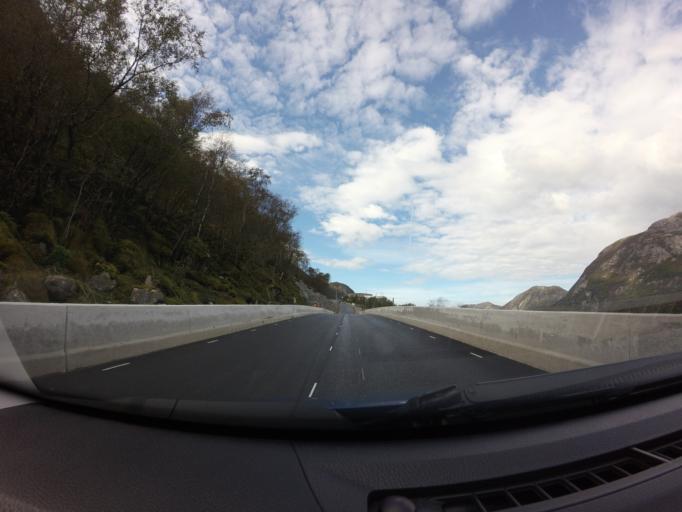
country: NO
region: Rogaland
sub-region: Forsand
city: Forsand
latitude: 58.8355
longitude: 6.1740
